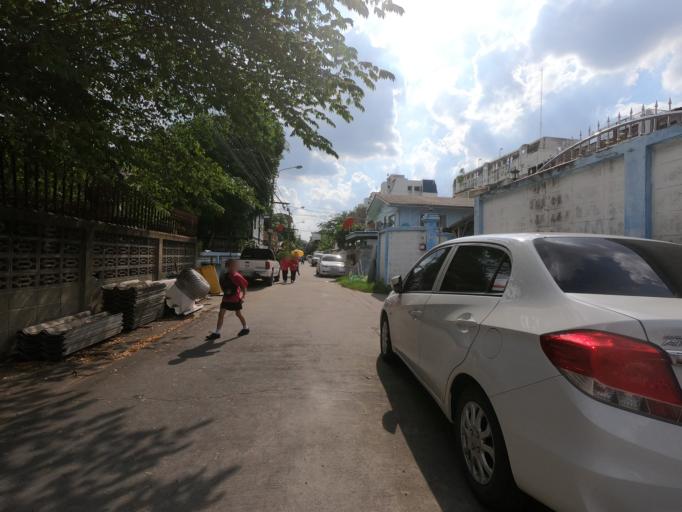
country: TH
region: Bangkok
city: Lat Phrao
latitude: 13.8237
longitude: 100.6164
